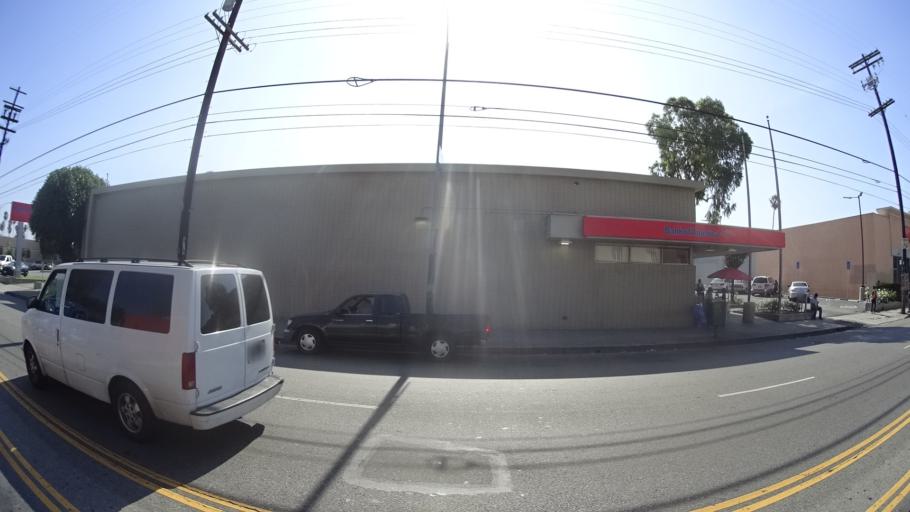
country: US
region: California
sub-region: Los Angeles County
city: Echo Park
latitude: 34.0483
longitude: -118.2917
